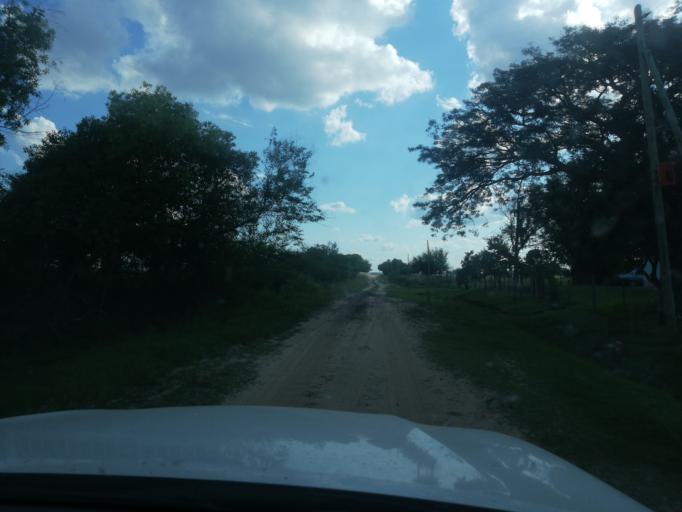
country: AR
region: Corrientes
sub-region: Departamento de San Miguel
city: San Miguel
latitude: -27.9903
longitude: -57.5693
